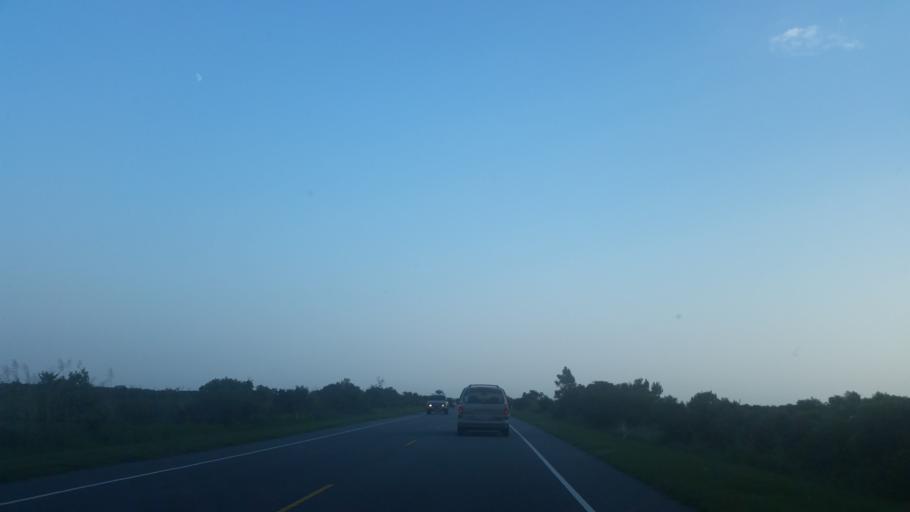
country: US
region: North Carolina
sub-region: Dare County
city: Wanchese
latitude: 35.8931
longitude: -75.5942
